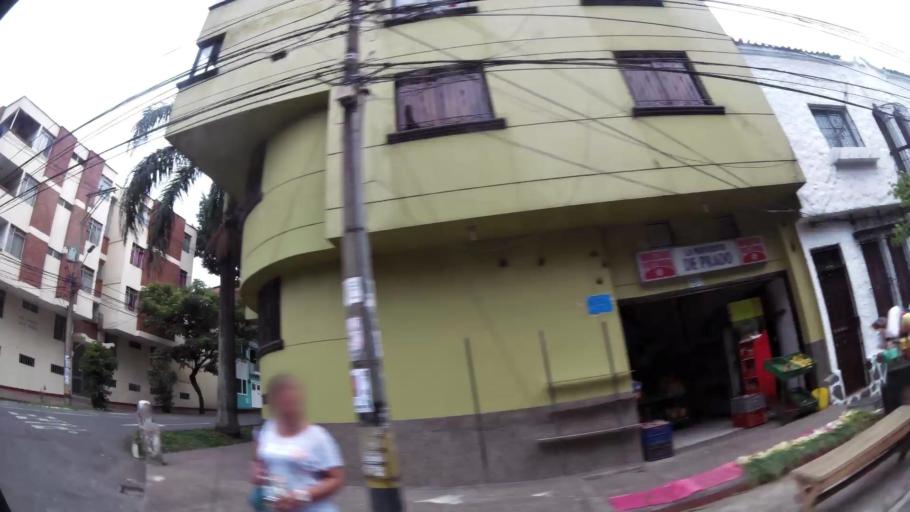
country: CO
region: Antioquia
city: Medellin
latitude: 6.2583
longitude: -75.5616
